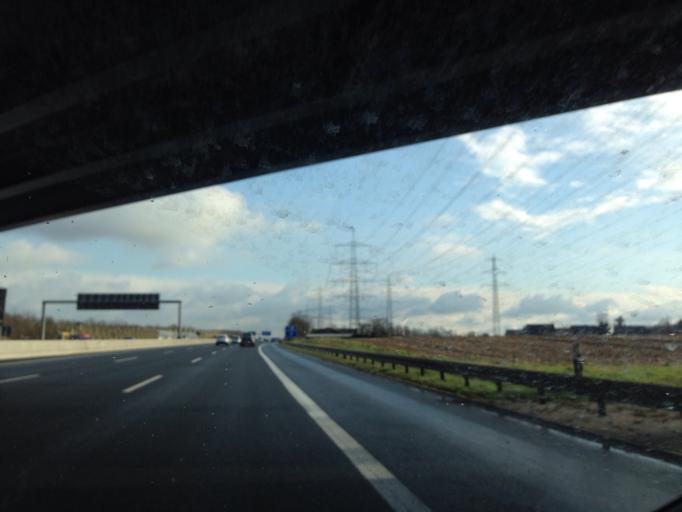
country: DE
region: North Rhine-Westphalia
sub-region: Regierungsbezirk Dusseldorf
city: Kaarst
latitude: 51.2108
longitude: 6.6468
